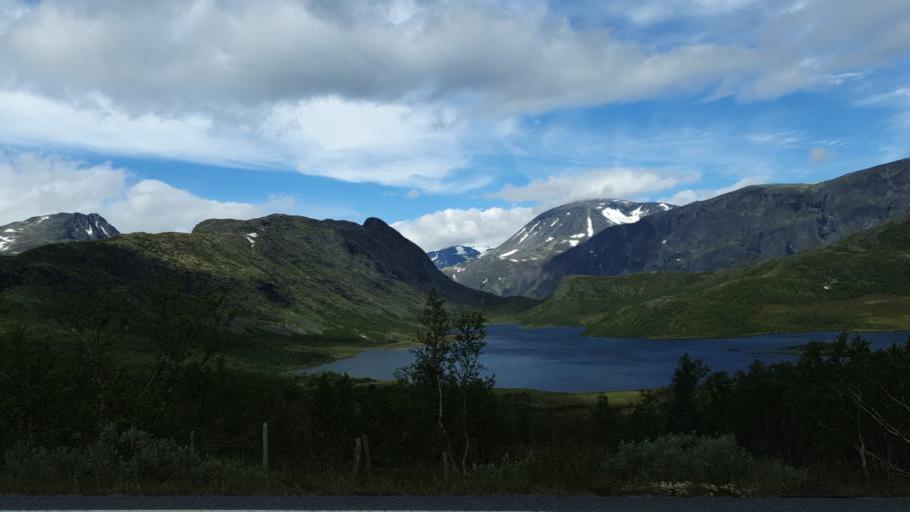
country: NO
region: Oppland
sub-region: Oystre Slidre
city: Heggenes
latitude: 61.4688
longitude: 8.8147
